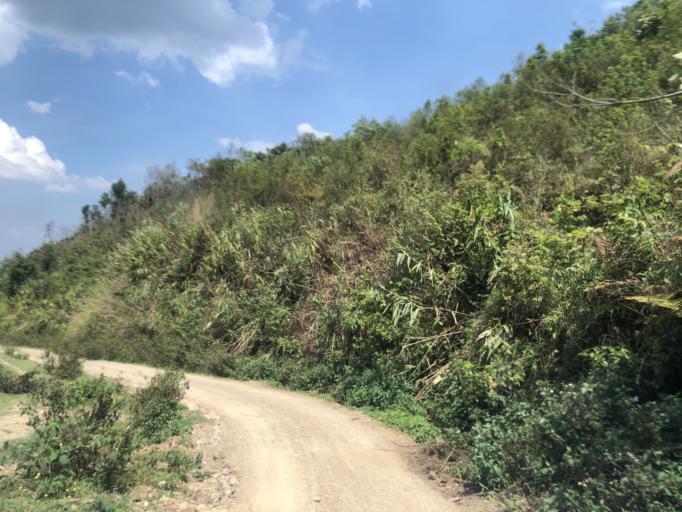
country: LA
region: Phongsali
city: Phongsali
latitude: 21.3973
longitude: 102.2201
